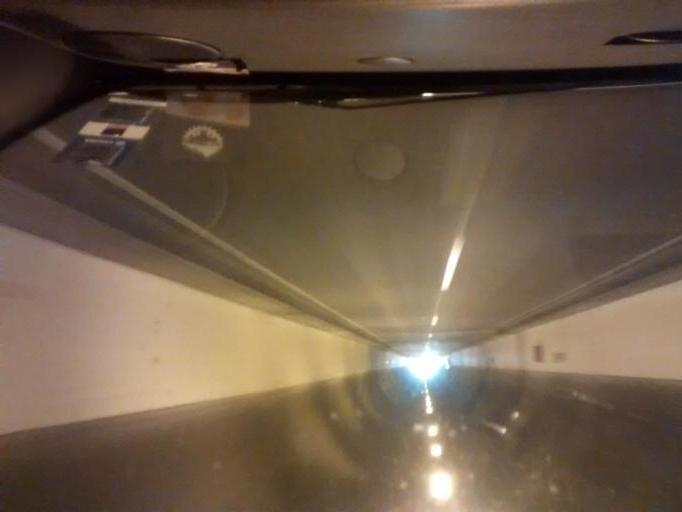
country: PT
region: Madeira
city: Calheta
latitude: 32.7265
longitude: -17.1738
